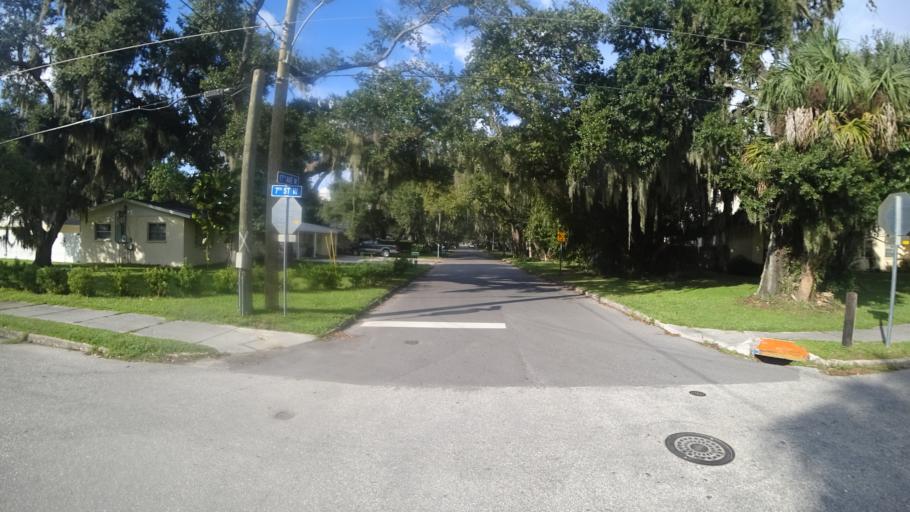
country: US
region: Florida
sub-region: Manatee County
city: Palmetto
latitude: 27.5176
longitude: -82.5852
